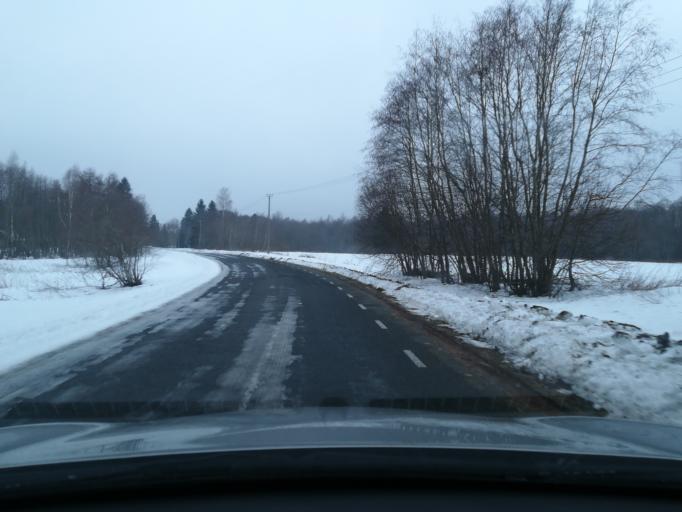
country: EE
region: Harju
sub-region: Loksa linn
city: Loksa
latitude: 59.4677
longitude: 25.7010
